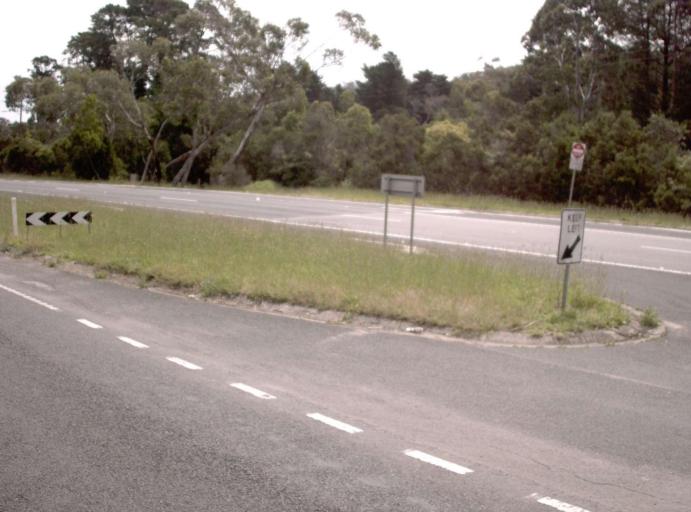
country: AU
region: Victoria
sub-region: Mornington Peninsula
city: Moorooduc
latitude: -38.2054
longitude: 145.1177
